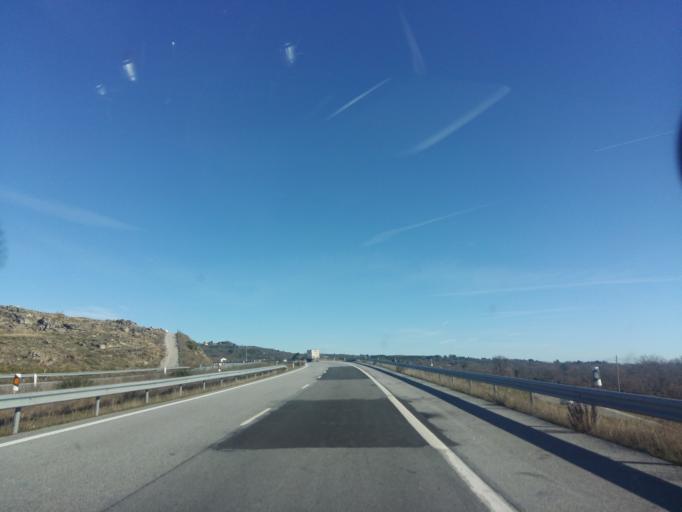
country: PT
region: Guarda
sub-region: Guarda
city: Sequeira
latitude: 40.5817
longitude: -7.1595
